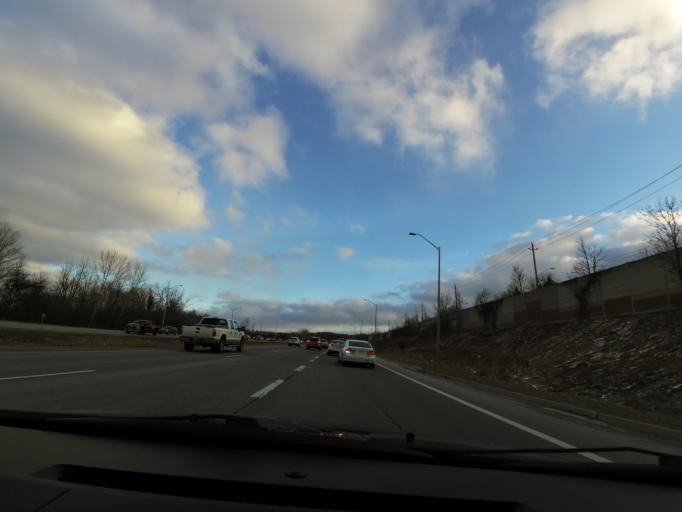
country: CA
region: Ontario
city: Waterloo
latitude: 43.4824
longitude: -80.4996
